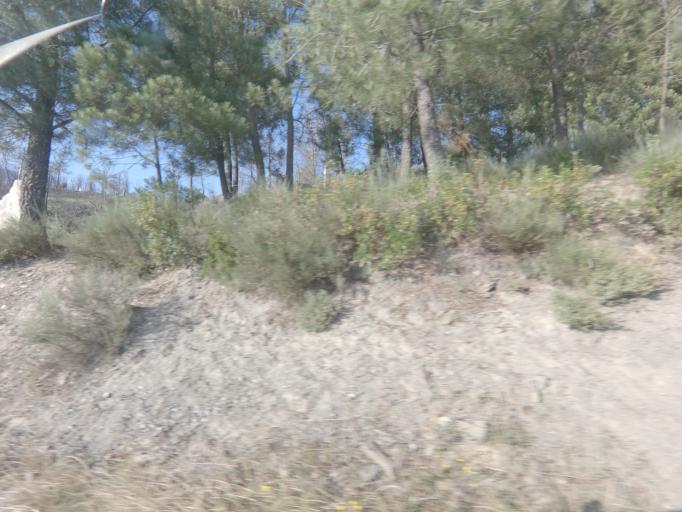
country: PT
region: Vila Real
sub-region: Sabrosa
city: Vilela
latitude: 41.1867
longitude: -7.6157
